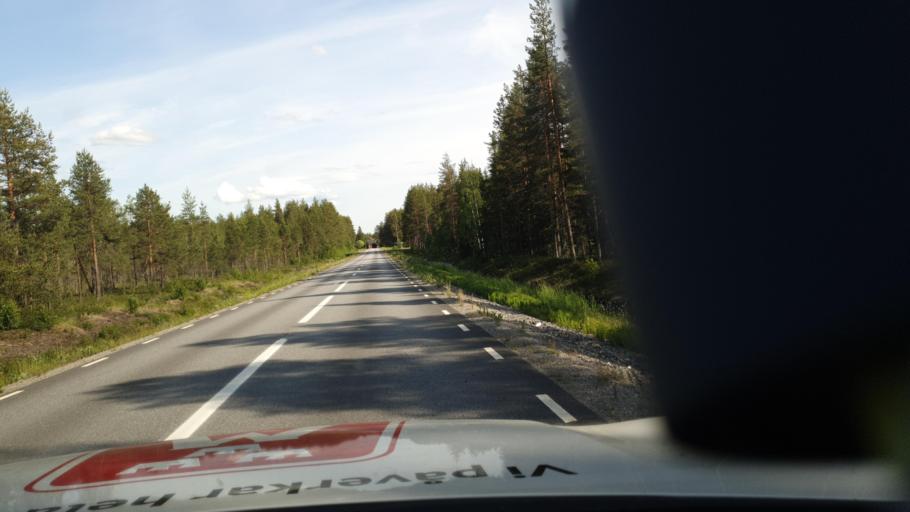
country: SE
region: Vaesterbotten
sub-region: Skelleftea Kommun
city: Forsbacka
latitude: 64.7323
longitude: 20.3904
